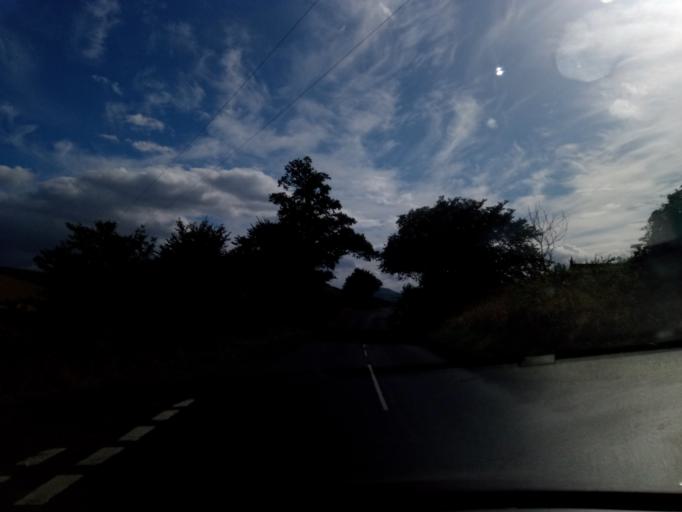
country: GB
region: Scotland
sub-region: The Scottish Borders
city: Coldstream
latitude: 55.5601
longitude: -2.2666
